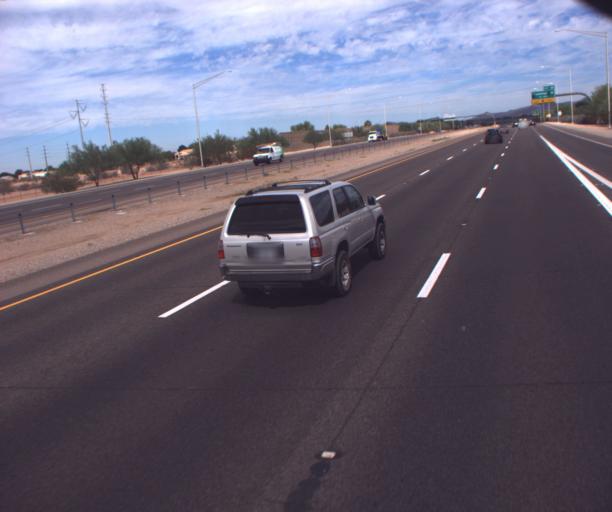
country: US
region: Arizona
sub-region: Maricopa County
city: Queen Creek
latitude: 33.3553
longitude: -111.6438
